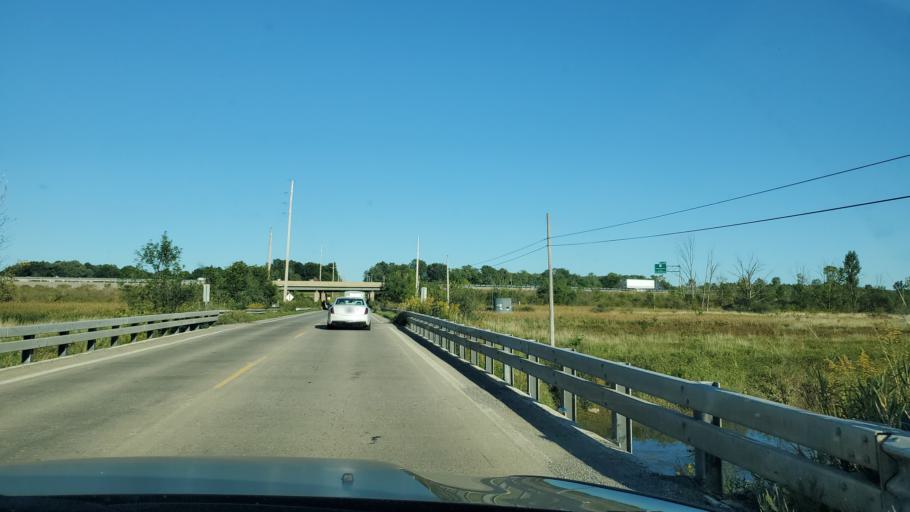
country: US
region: Ohio
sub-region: Mahoning County
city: Boardman
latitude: 40.9880
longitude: -80.6903
